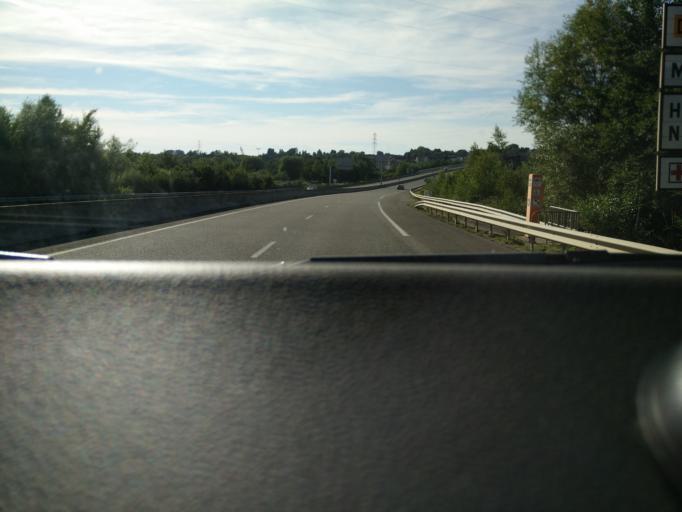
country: FR
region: Nord-Pas-de-Calais
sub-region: Departement du Nord
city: Hautmont
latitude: 50.2604
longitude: 3.9308
